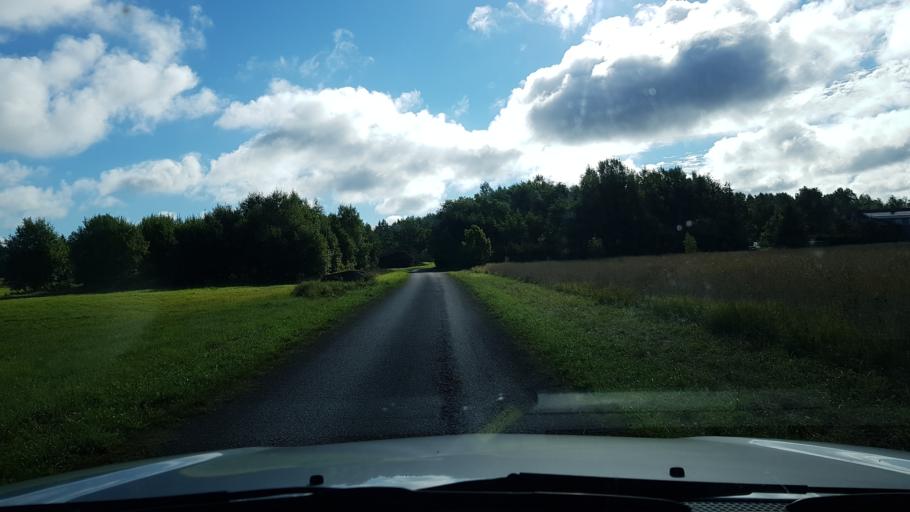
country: EE
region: Harju
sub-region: Rae vald
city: Vaida
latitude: 59.2515
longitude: 25.0221
